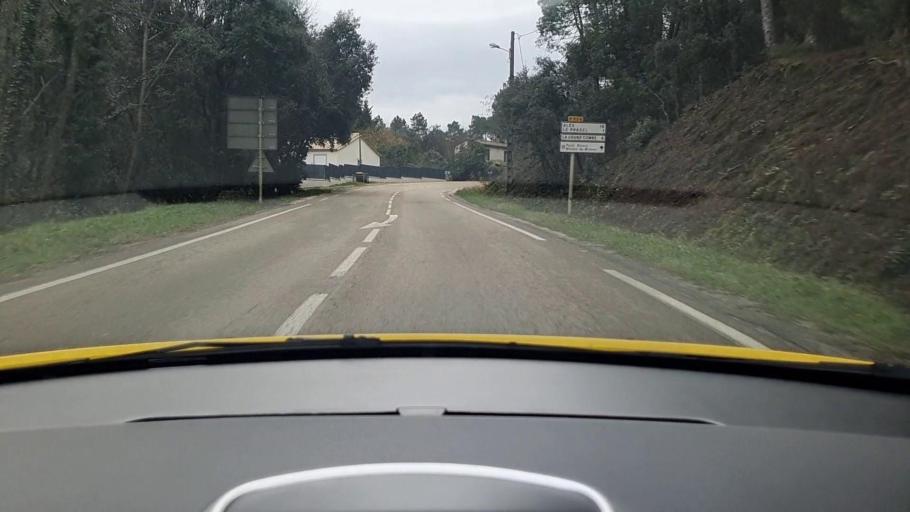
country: FR
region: Languedoc-Roussillon
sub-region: Departement du Gard
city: Laval-Pradel
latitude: 44.2426
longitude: 4.0532
